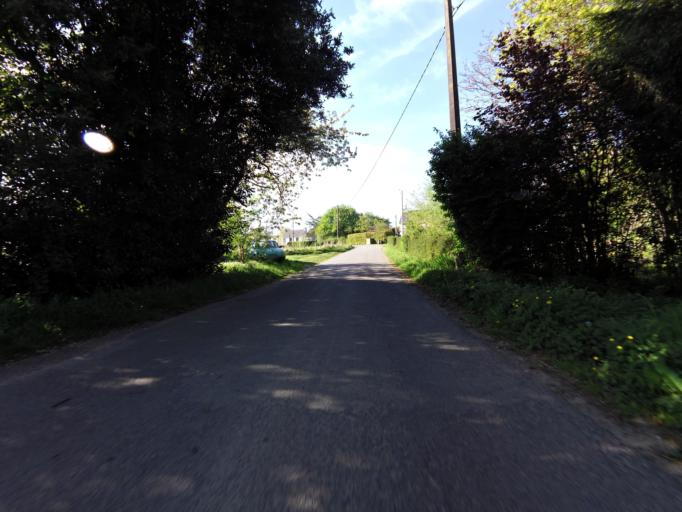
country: FR
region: Brittany
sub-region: Departement du Morbihan
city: Molac
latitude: 47.7305
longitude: -2.4553
